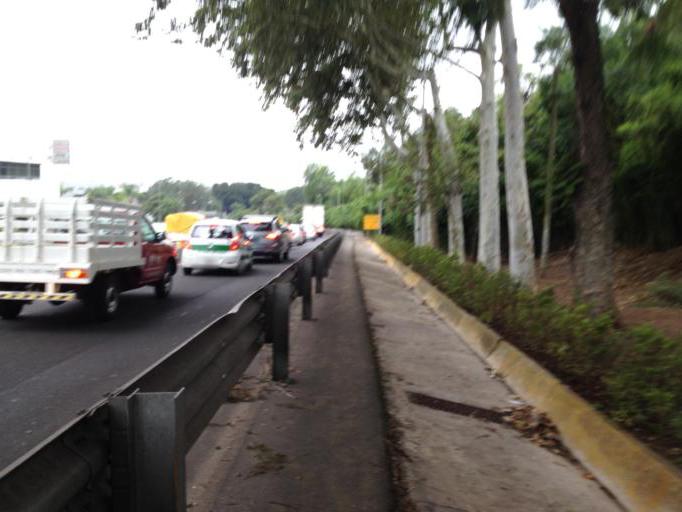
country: MX
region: Veracruz
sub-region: Xalapa
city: Xalapa de Enriquez
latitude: 19.5252
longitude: -96.8973
